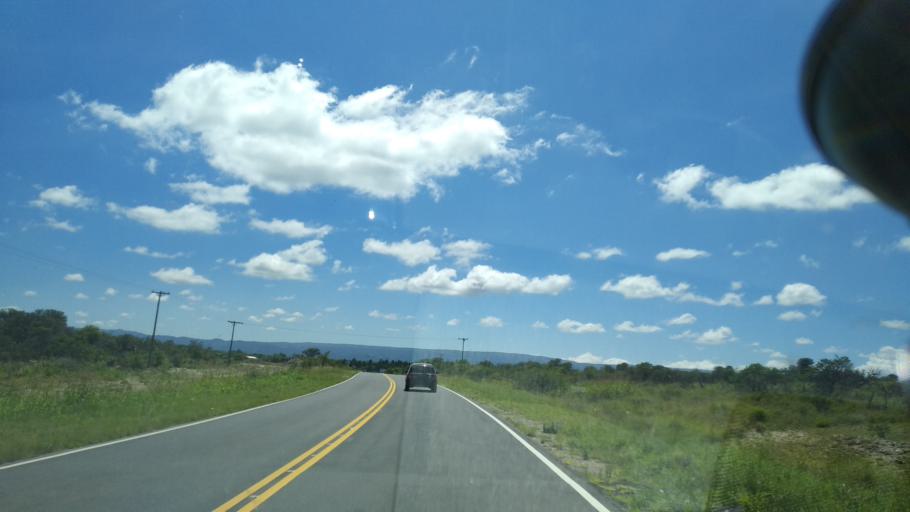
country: AR
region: Cordoba
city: Salsacate
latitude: -31.3503
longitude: -65.0871
